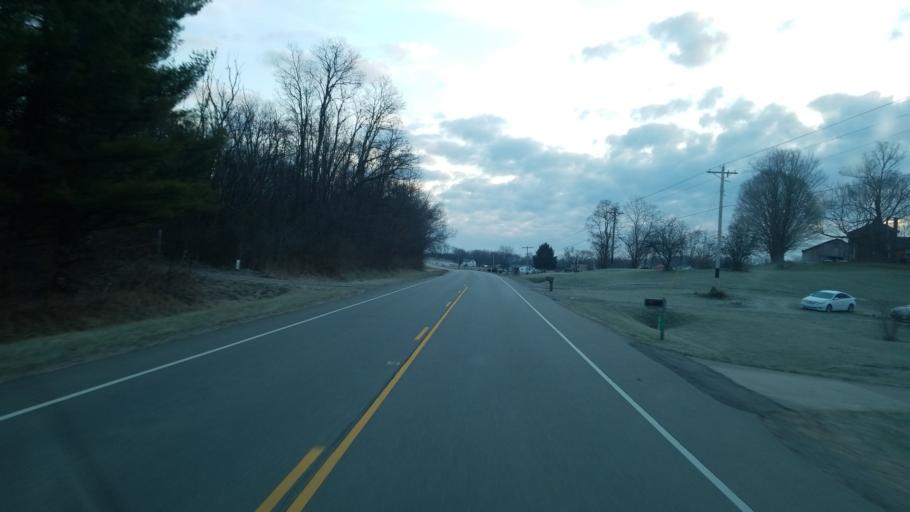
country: US
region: Ohio
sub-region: Highland County
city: Greenfield
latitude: 39.2281
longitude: -83.3783
